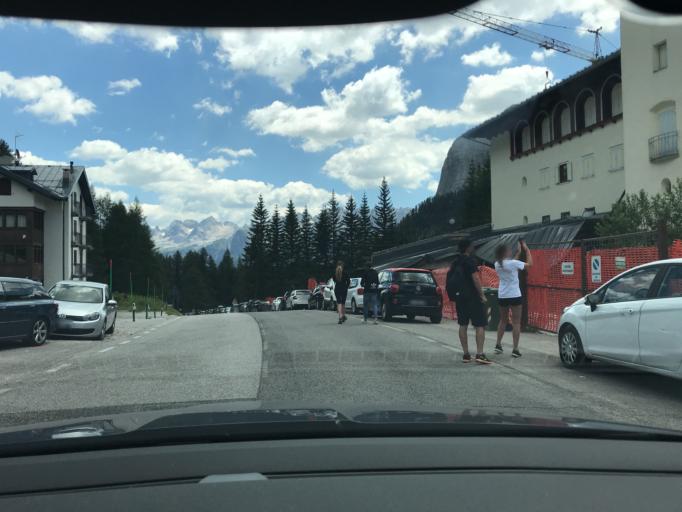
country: IT
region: Veneto
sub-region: Provincia di Belluno
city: Cortina d'Ampezzo
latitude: 46.5570
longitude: 12.2019
